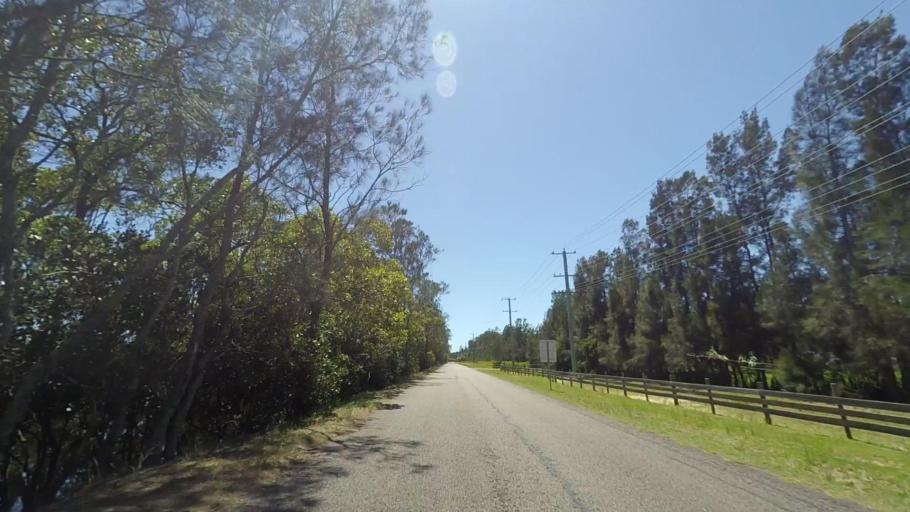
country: AU
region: New South Wales
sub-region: Port Stephens Shire
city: Medowie
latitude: -32.7794
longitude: 151.9605
